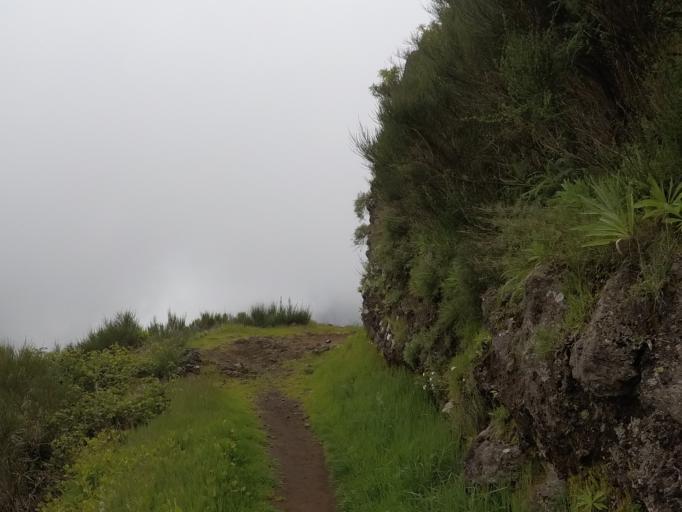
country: PT
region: Madeira
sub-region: Camara de Lobos
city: Curral das Freiras
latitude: 32.7162
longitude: -16.9897
